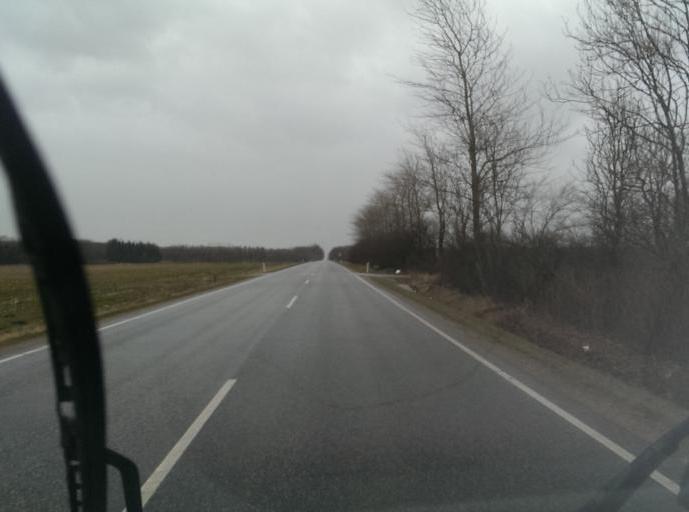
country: DK
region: Central Jutland
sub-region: Ringkobing-Skjern Kommune
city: Skjern
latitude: 56.0830
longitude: 8.4143
